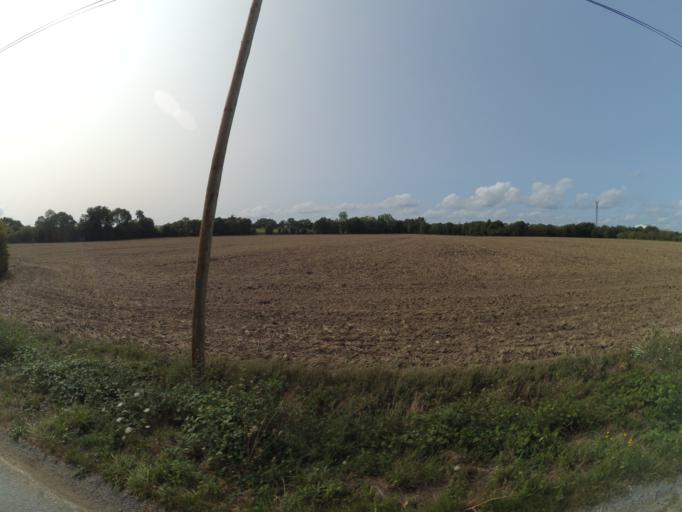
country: FR
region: Pays de la Loire
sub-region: Departement de la Vendee
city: Treize-Septiers
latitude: 46.9770
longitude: -1.2233
